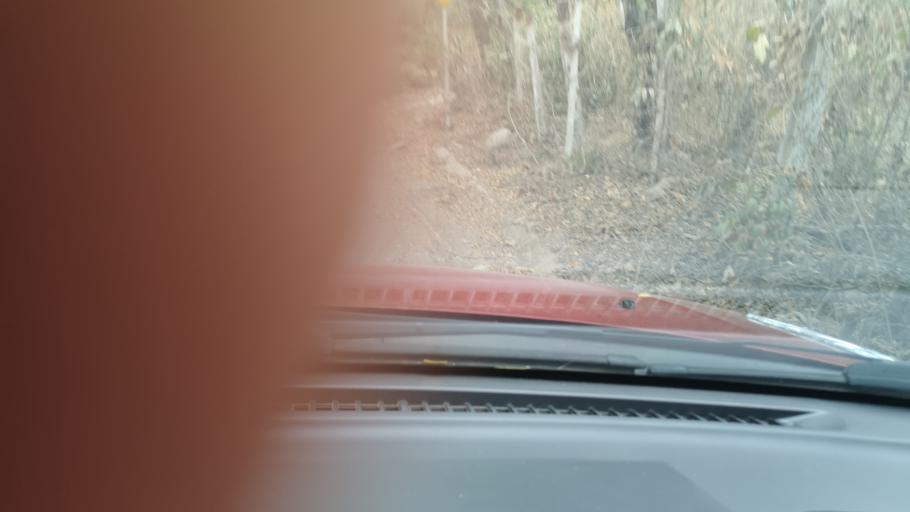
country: CO
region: Huila
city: Neiva
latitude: 2.9577
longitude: -75.3285
